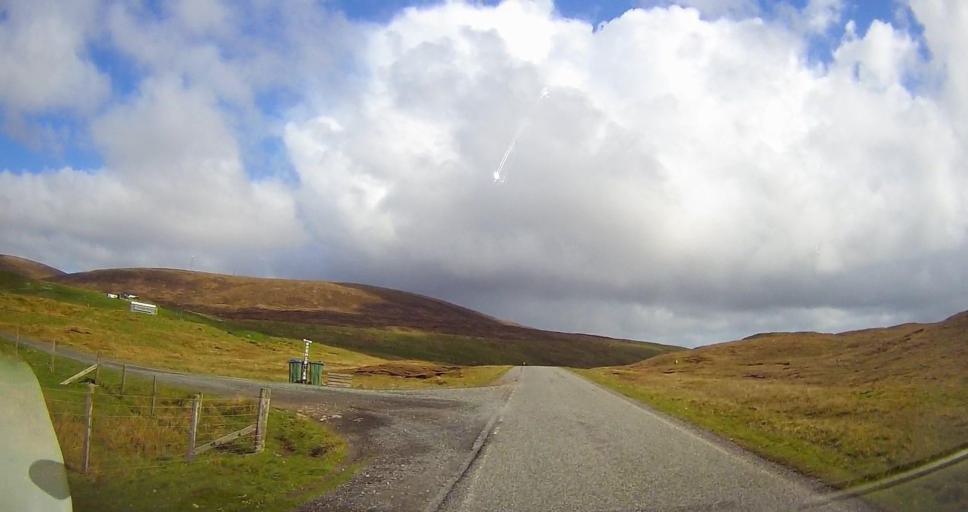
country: GB
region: Scotland
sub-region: Shetland Islands
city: Lerwick
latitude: 60.5191
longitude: -1.3772
